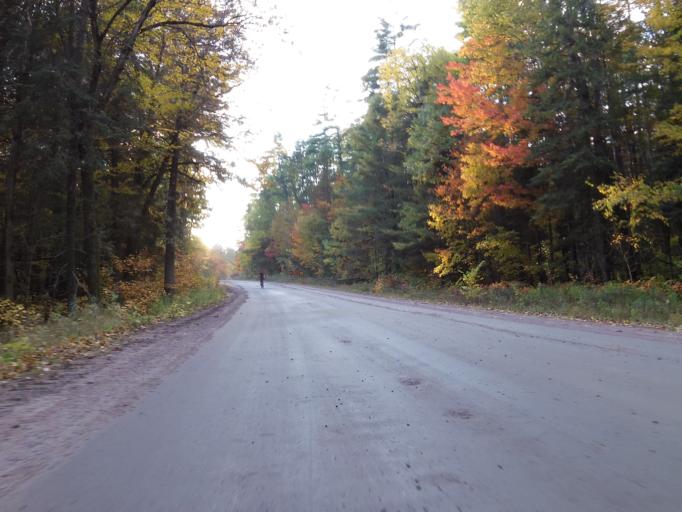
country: CA
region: Ontario
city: Deep River
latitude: 45.8901
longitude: -77.6341
